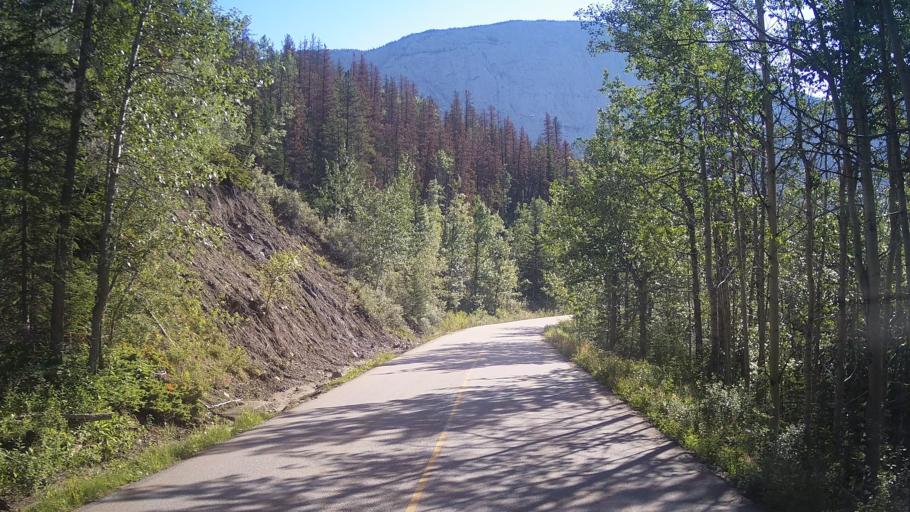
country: CA
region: Alberta
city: Hinton
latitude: 53.1775
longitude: -117.8505
